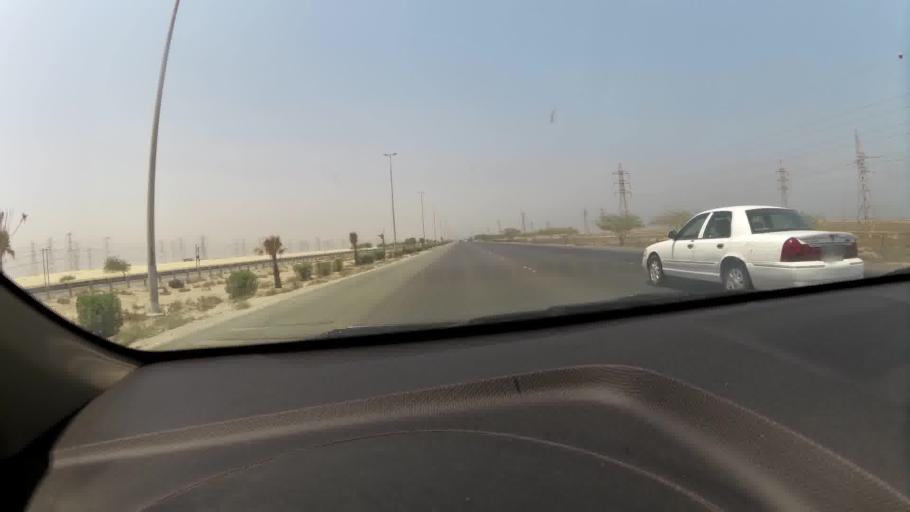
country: KW
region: Al Ahmadi
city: Al Fahahil
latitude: 28.8371
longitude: 48.2516
